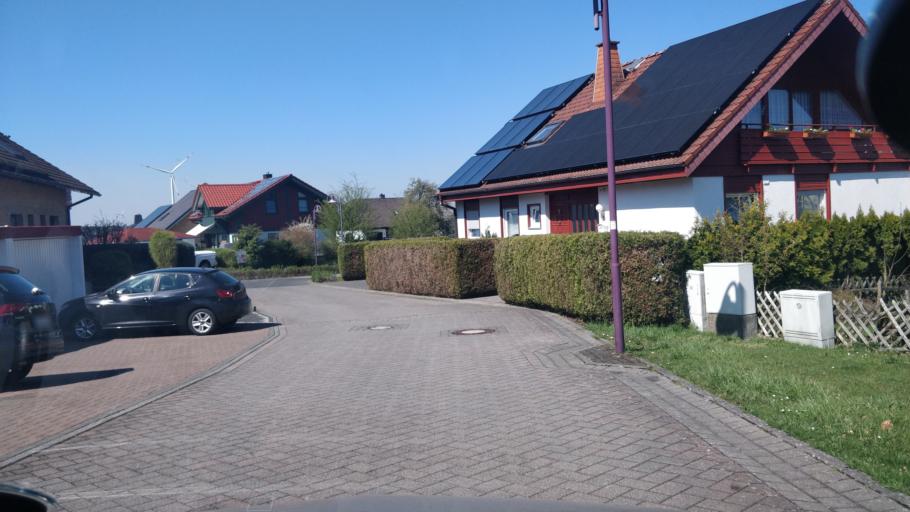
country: DE
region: Rheinland-Pfalz
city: Niederrossbach
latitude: 50.6288
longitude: 8.0392
